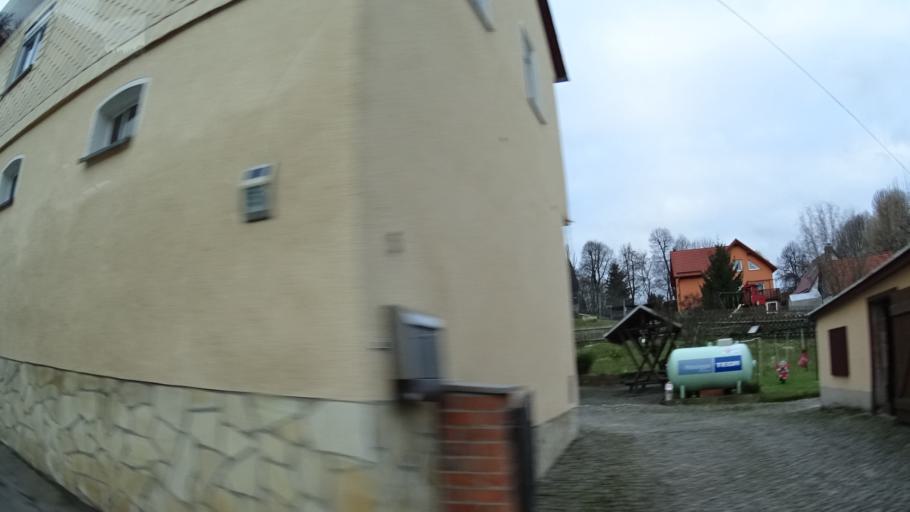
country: DE
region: Thuringia
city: Lemnitz
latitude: 50.7217
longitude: 11.8341
